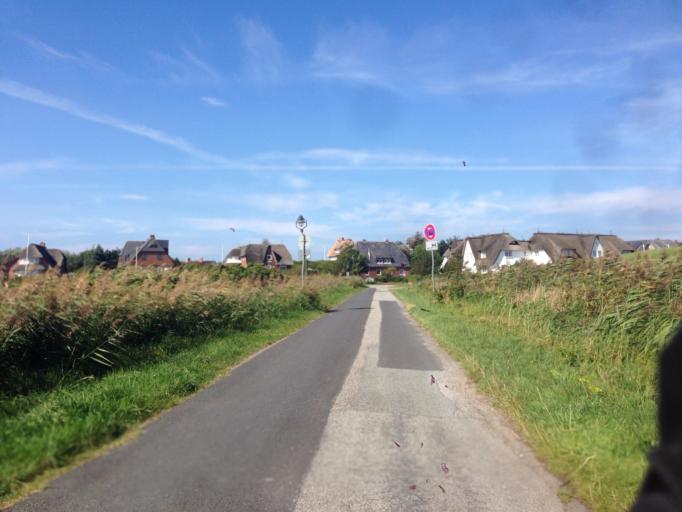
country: DE
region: Schleswig-Holstein
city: Westerland
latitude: 54.8468
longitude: 8.2964
